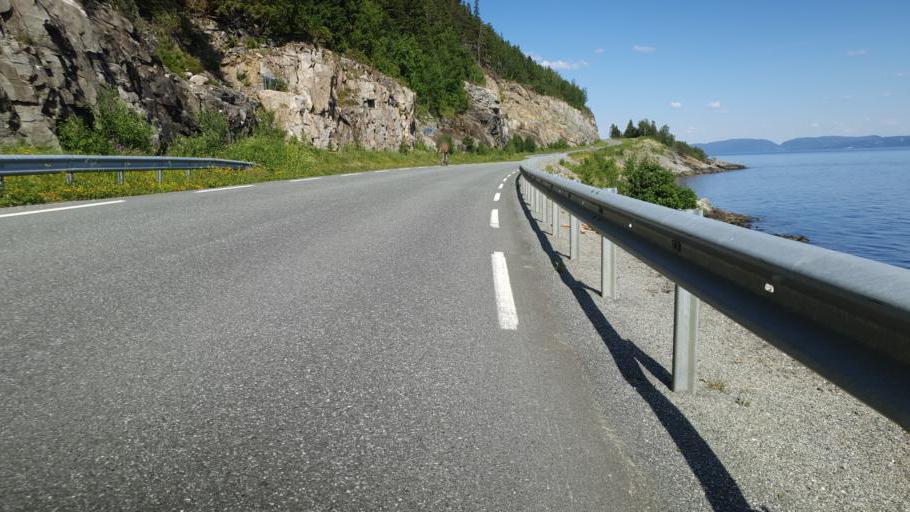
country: NO
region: Nord-Trondelag
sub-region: Leksvik
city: Leksvik
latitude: 63.6090
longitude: 10.4955
